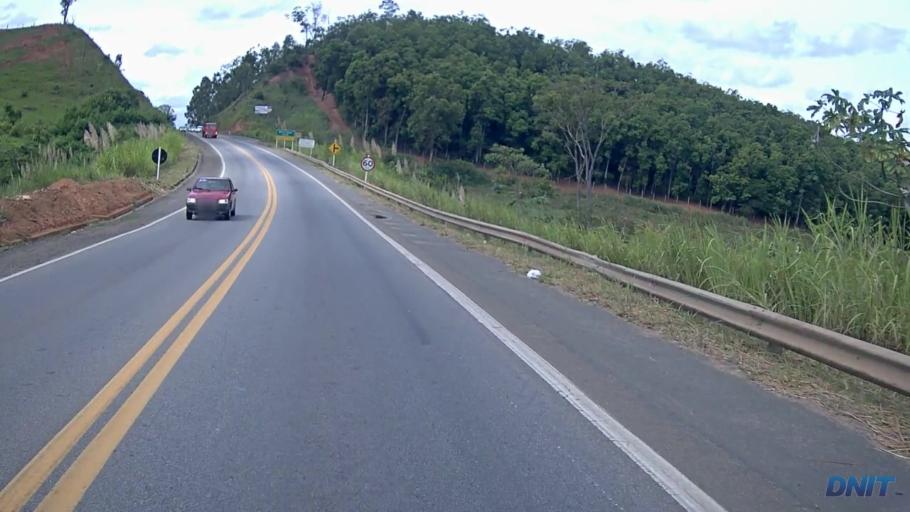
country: BR
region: Minas Gerais
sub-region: Ipatinga
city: Ipatinga
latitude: -19.4482
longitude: -42.5151
